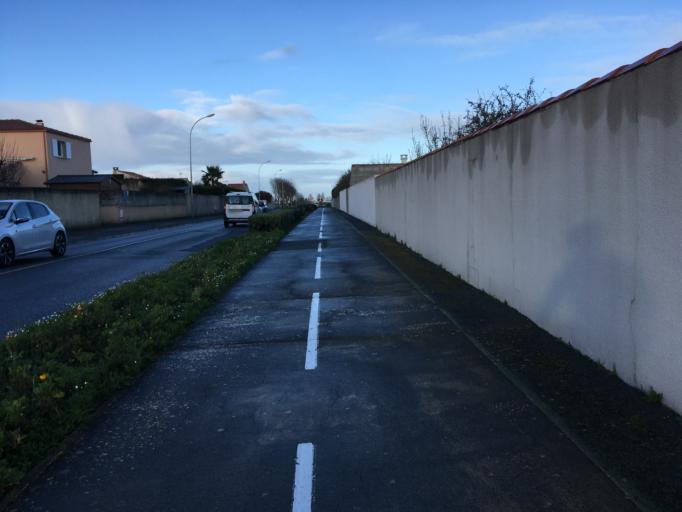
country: FR
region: Poitou-Charentes
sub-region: Departement de la Charente-Maritime
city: Nieul-sur-Mer
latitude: 46.2006
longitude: -1.1639
